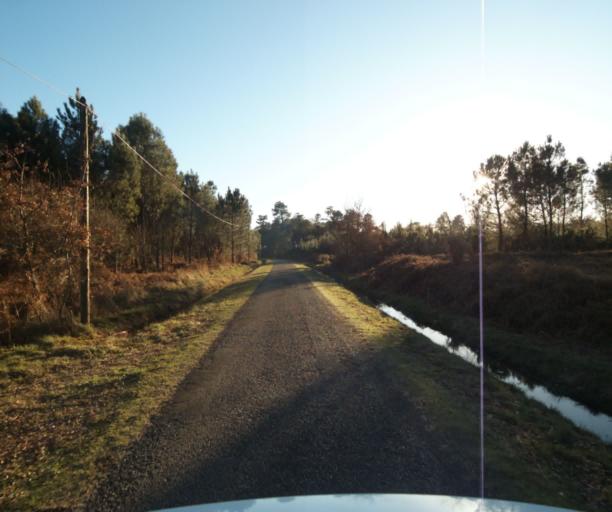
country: FR
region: Aquitaine
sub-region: Departement des Landes
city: Gabarret
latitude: 44.1062
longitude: -0.0792
